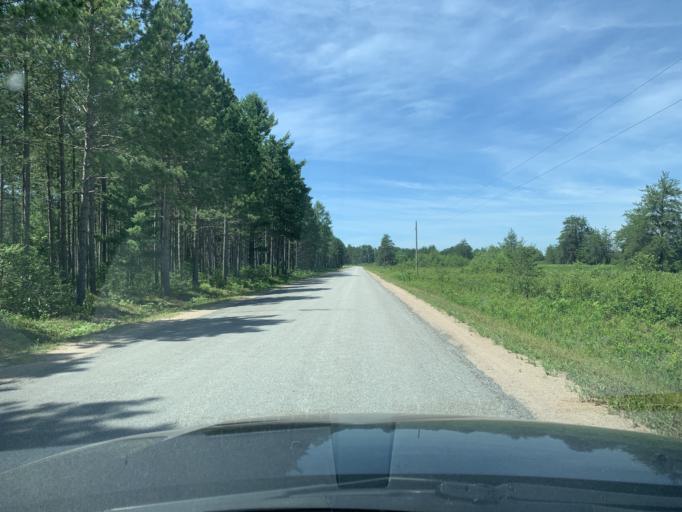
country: CA
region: Ontario
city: Petawawa
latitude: 45.6601
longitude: -77.5862
